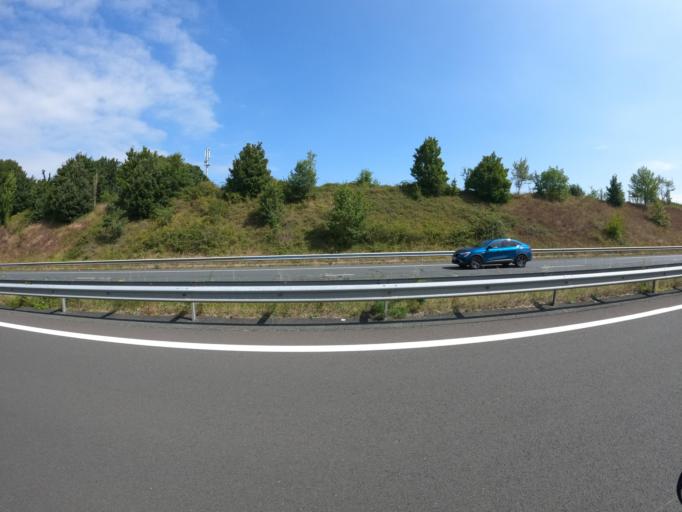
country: FR
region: Poitou-Charentes
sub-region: Departement de la Charente-Maritime
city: Courcon
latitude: 46.2150
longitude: -0.7695
